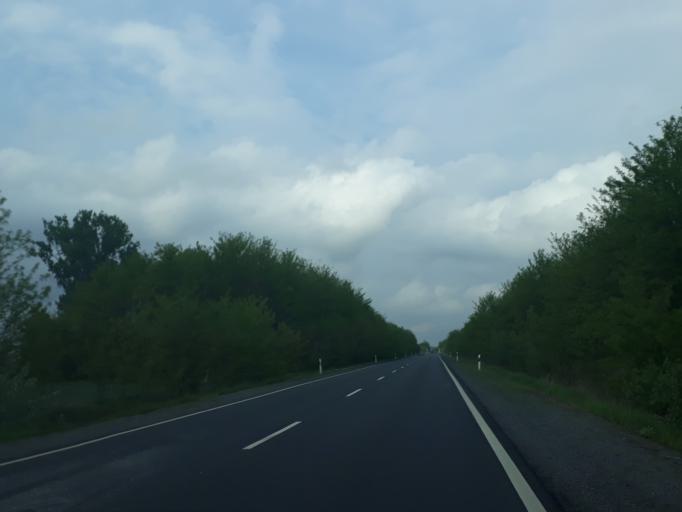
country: HU
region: Szabolcs-Szatmar-Bereg
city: Nyirtass
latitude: 48.1302
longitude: 22.0136
